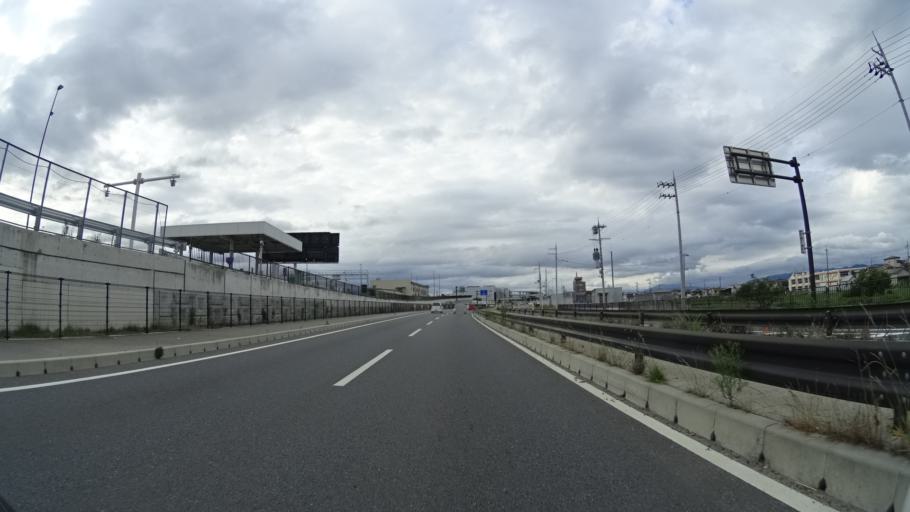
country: JP
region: Kyoto
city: Tanabe
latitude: 34.8499
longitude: 135.7623
